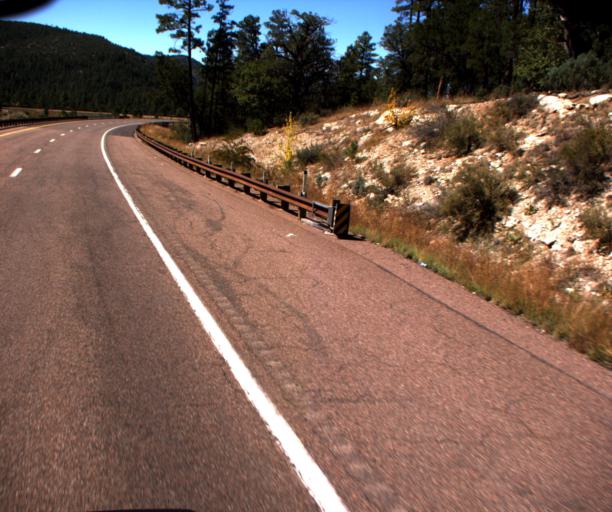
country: US
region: Arizona
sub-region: Gila County
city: Star Valley
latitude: 34.3096
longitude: -111.0177
